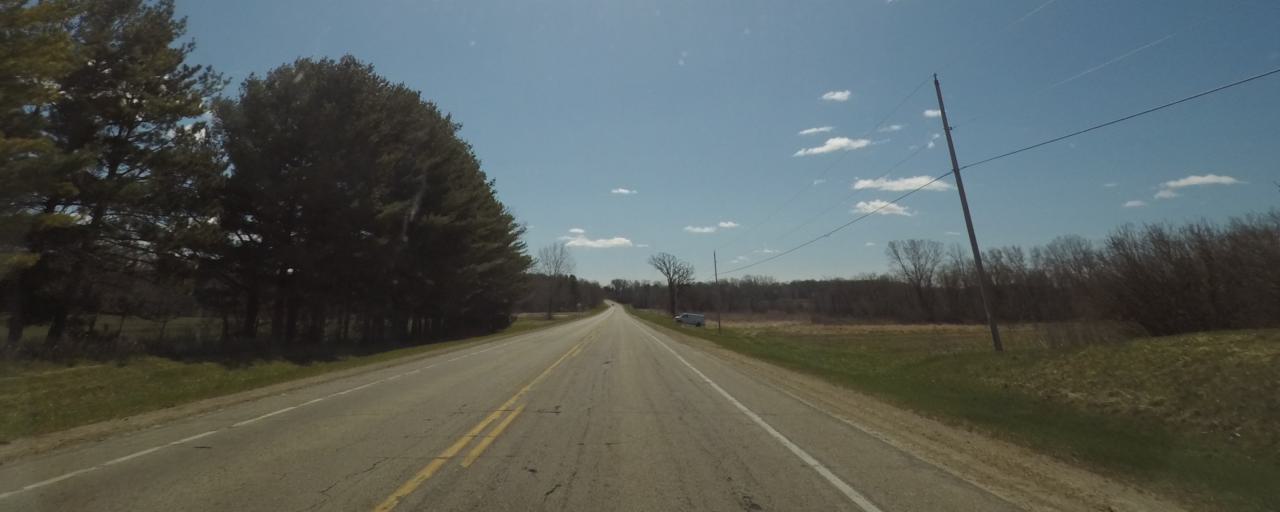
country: US
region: Wisconsin
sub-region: Dane County
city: Cottage Grove
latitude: 43.0876
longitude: -89.1670
